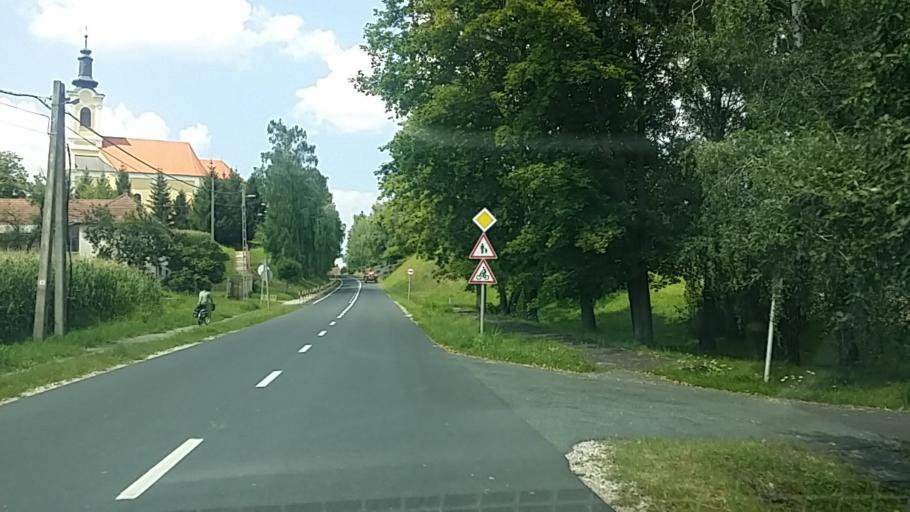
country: HR
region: Medimurska
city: Podturen
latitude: 46.5195
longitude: 16.5563
